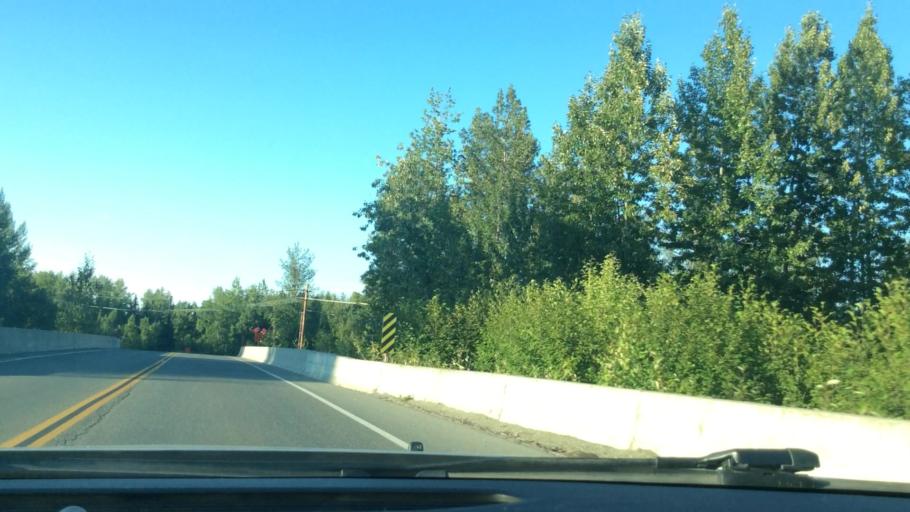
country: US
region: Alaska
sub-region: Anchorage Municipality
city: Elmendorf Air Force Base
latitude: 61.2407
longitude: -149.7080
